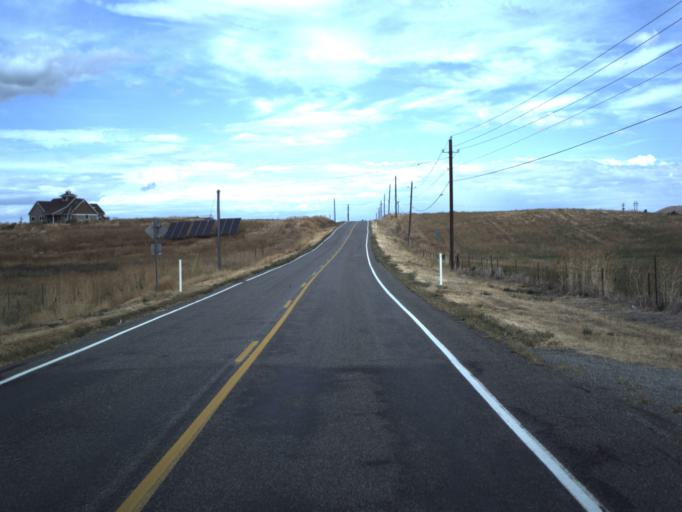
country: US
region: Utah
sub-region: Cache County
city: Benson
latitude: 41.8463
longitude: -112.0021
